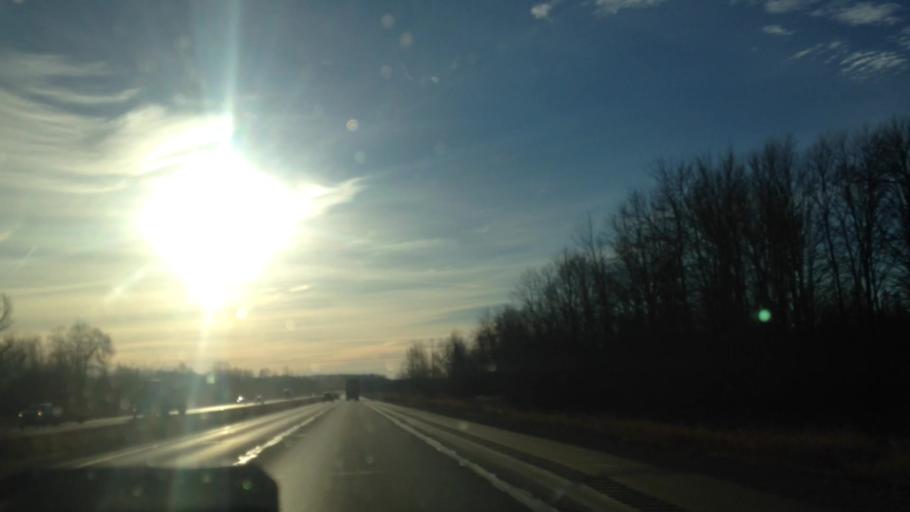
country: US
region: Wisconsin
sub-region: Dodge County
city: Theresa
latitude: 43.4515
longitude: -88.3556
